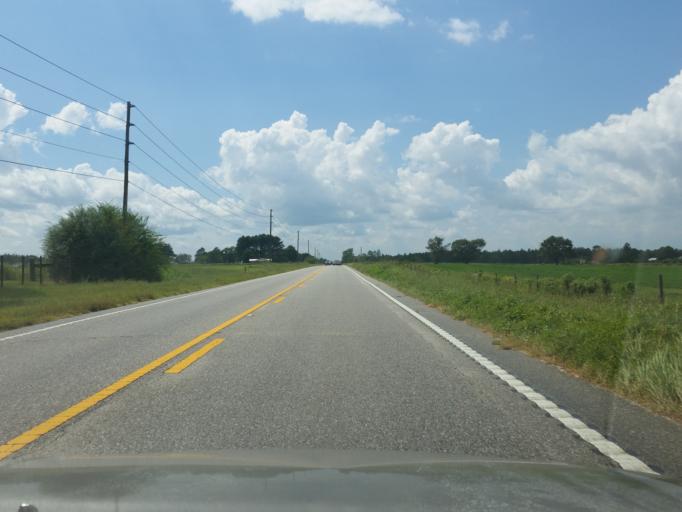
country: US
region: Alabama
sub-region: Baldwin County
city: Elberta
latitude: 30.5388
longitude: -87.5442
